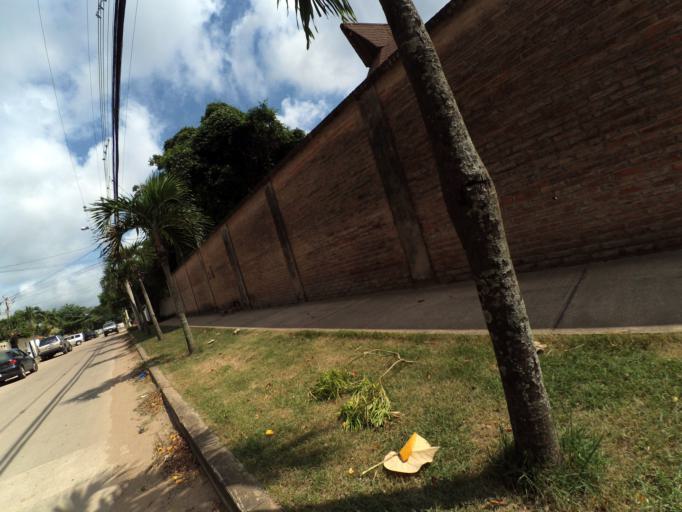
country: BO
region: Santa Cruz
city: Santa Cruz de la Sierra
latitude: -17.8084
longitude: -63.2271
